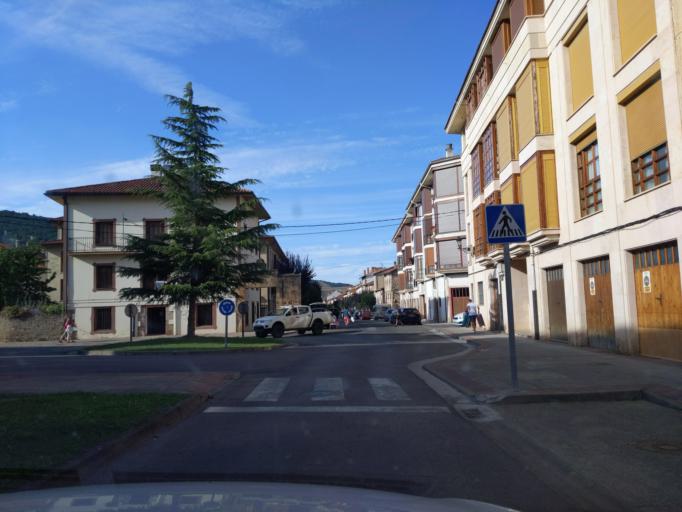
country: ES
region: La Rioja
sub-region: Provincia de La Rioja
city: Ezcaray
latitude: 42.3243
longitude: -3.0123
